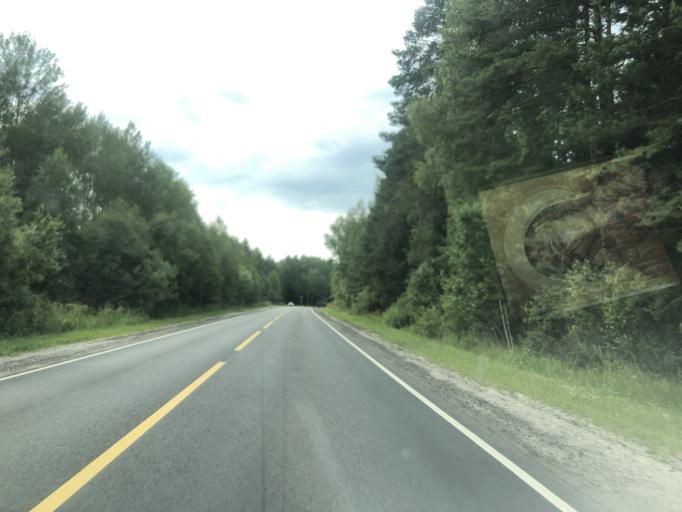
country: RU
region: Ivanovo
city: Verkhniy Landekh
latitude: 56.7399
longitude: 42.5328
